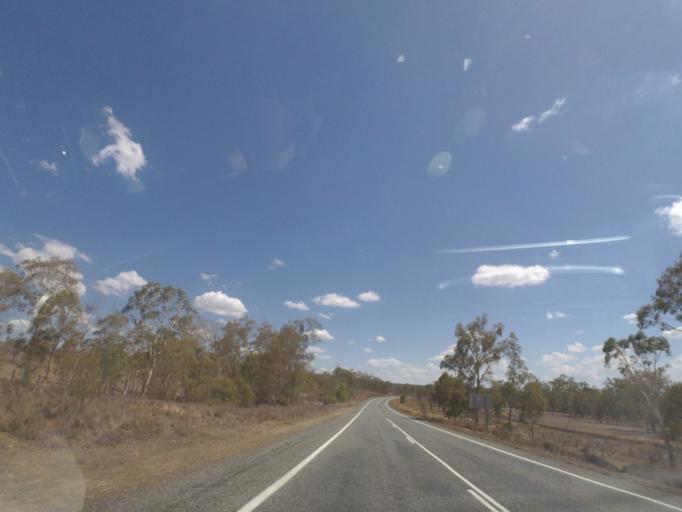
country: AU
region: Queensland
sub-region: Southern Downs
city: Warwick
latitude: -28.2118
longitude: 151.5643
